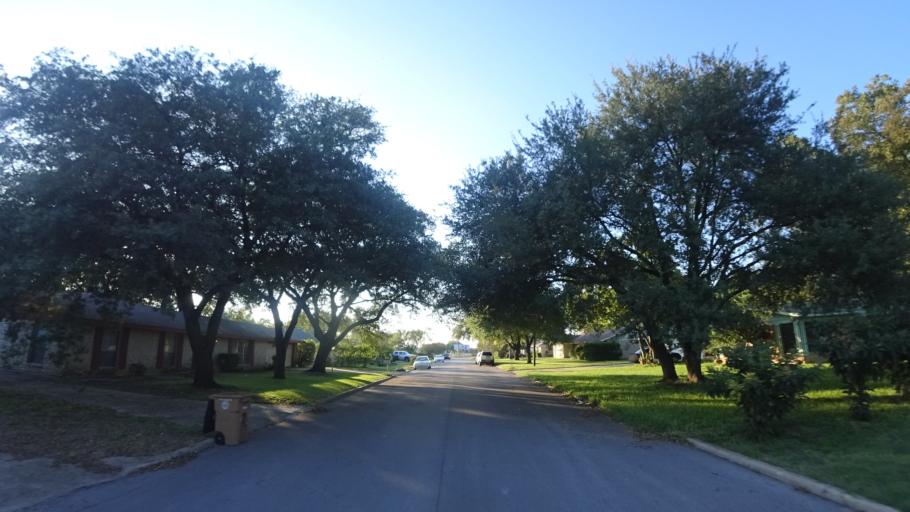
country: US
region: Texas
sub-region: Travis County
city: Wells Branch
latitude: 30.3670
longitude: -97.6796
